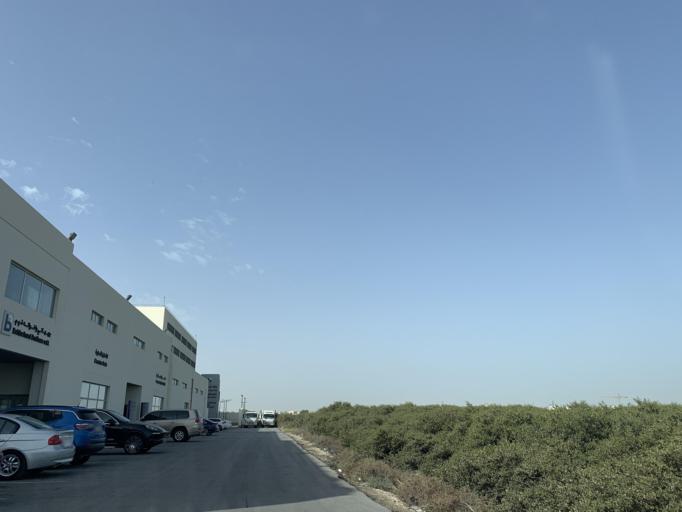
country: BH
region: Northern
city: Sitrah
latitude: 26.1544
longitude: 50.6084
